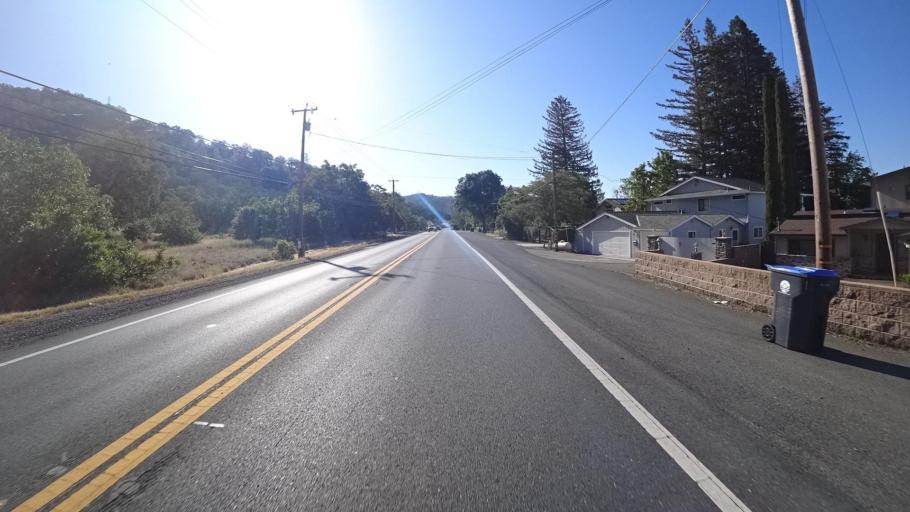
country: US
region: California
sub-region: Lake County
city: Nice
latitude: 39.1164
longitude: -122.8281
